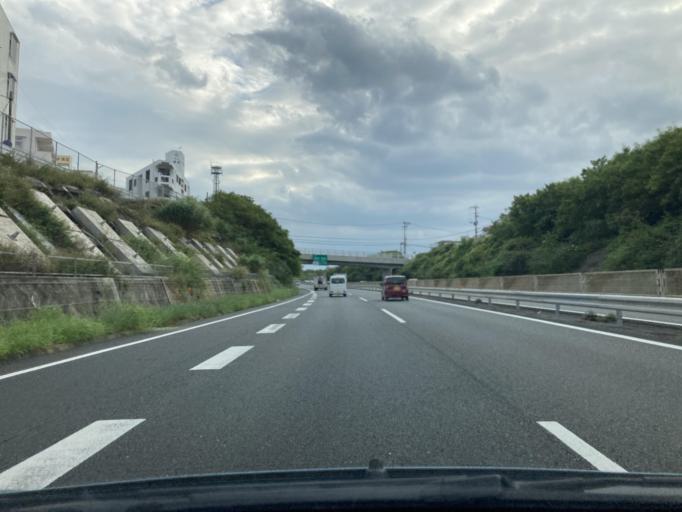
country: JP
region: Okinawa
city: Ginowan
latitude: 26.2548
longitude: 127.7629
